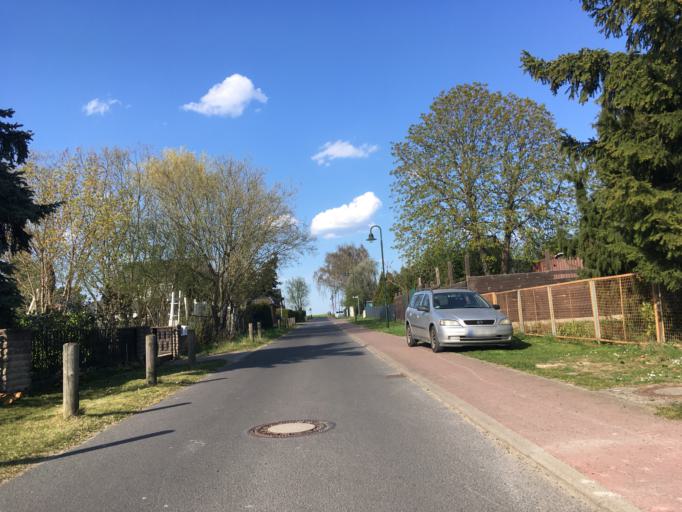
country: DE
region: Berlin
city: Falkenberg
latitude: 52.6006
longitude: 13.5489
